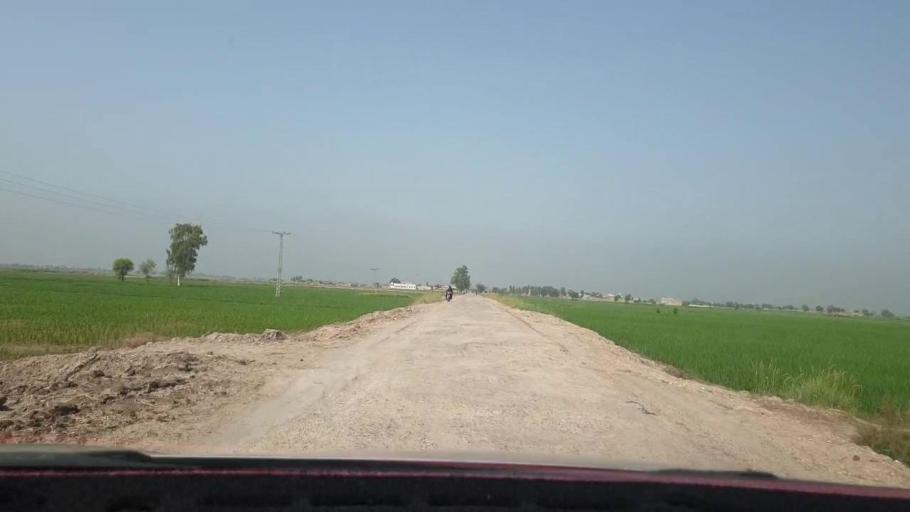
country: PK
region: Sindh
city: Nasirabad
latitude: 27.4239
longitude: 67.9189
